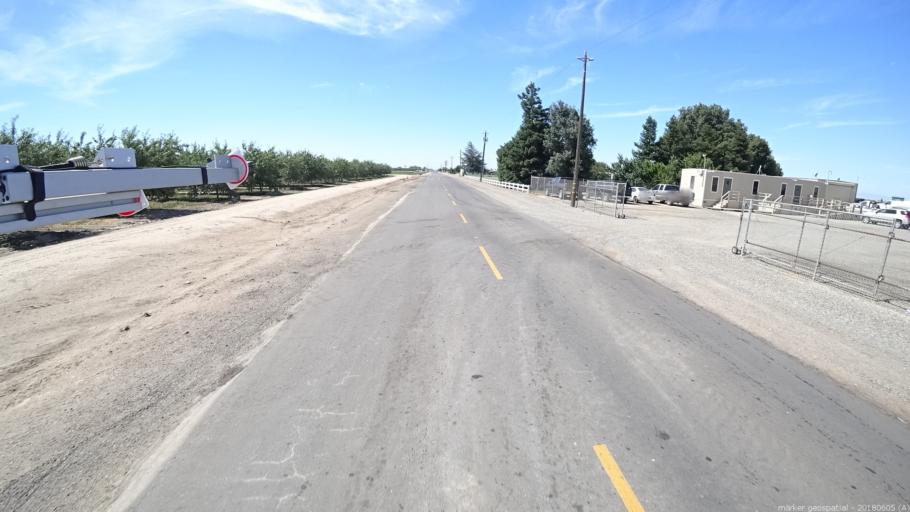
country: US
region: California
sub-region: Madera County
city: Chowchilla
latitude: 37.0917
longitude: -120.3826
